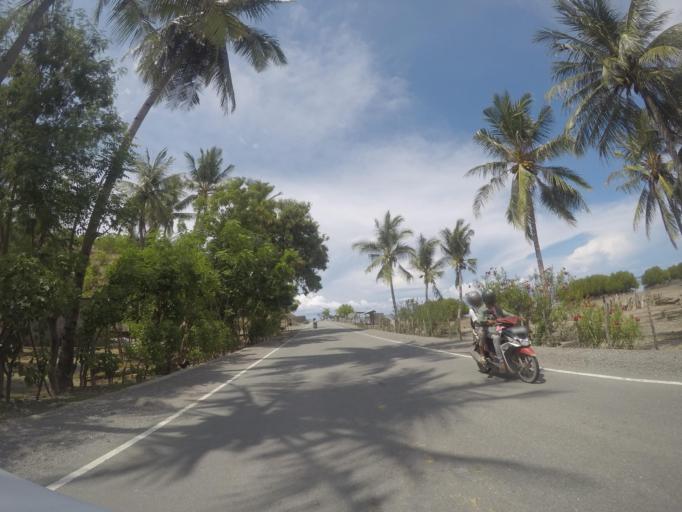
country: TL
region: Liquica
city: Liquica
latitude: -8.5716
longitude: 125.4449
